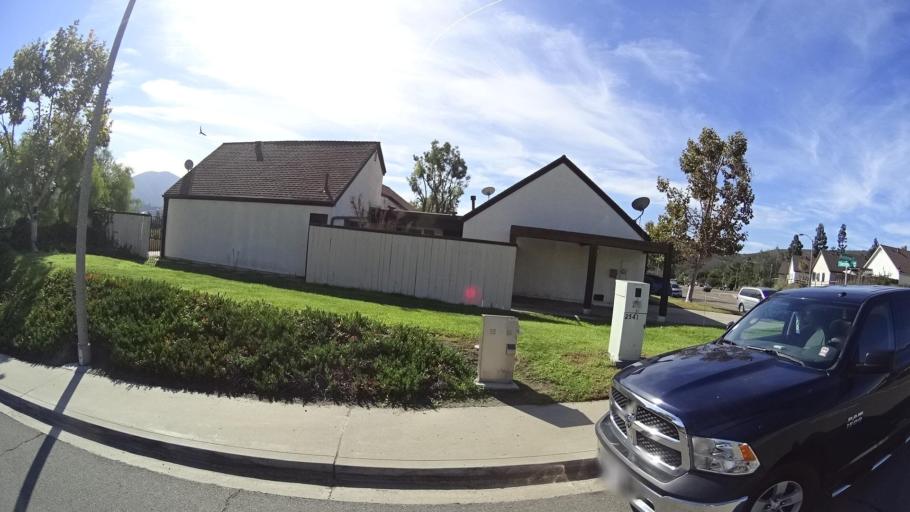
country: US
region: California
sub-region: San Diego County
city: Spring Valley
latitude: 32.7327
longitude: -116.9820
